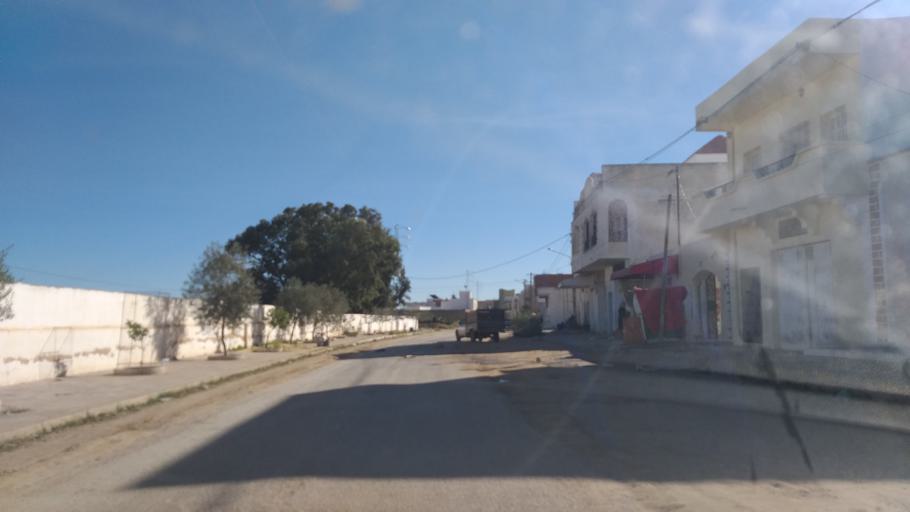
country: TN
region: Al Mahdiyah
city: El Jem
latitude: 35.2940
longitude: 10.7144
